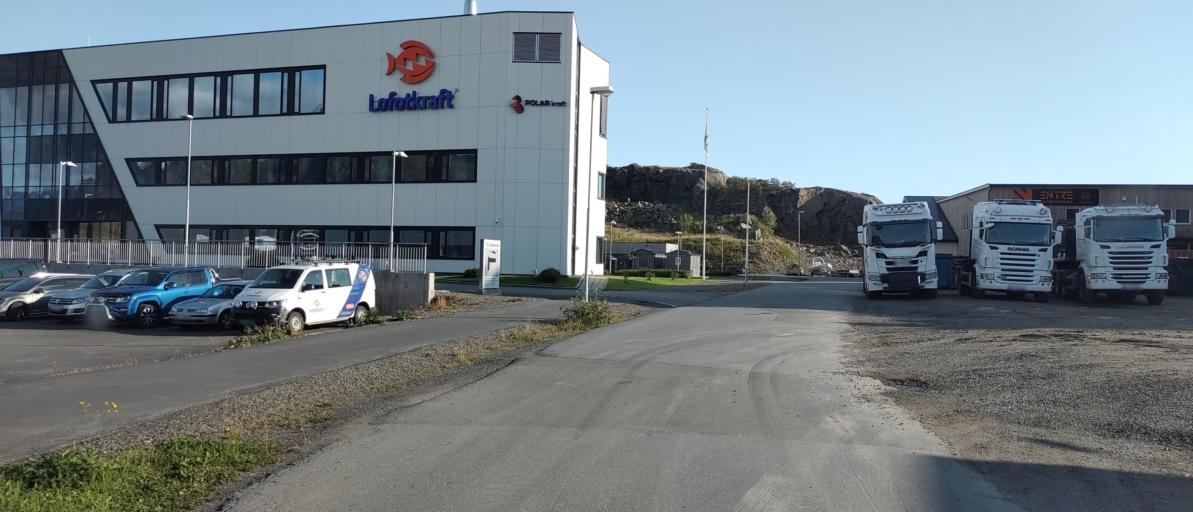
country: NO
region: Nordland
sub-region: Vagan
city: Svolvaer
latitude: 68.2258
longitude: 14.5553
